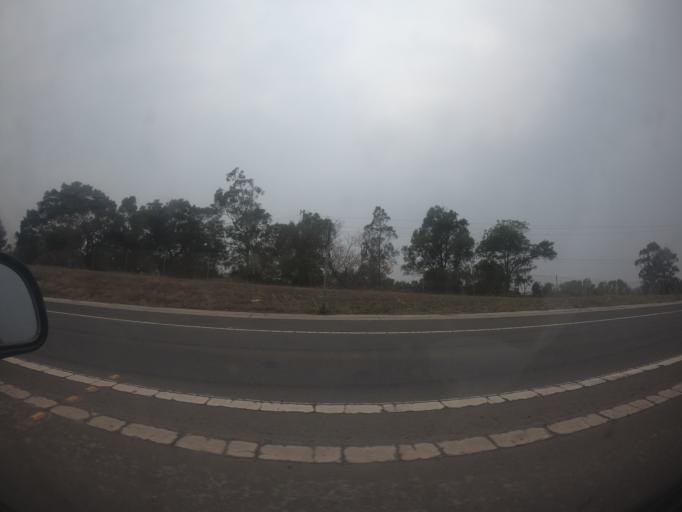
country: AU
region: New South Wales
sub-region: Shellharbour
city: Croom
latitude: -34.5915
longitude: 150.8485
